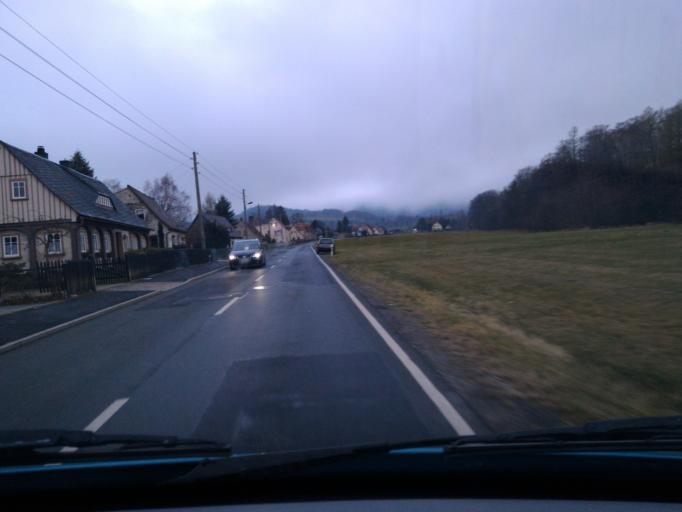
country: DE
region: Saxony
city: Grossschonau
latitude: 50.8813
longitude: 14.6590
